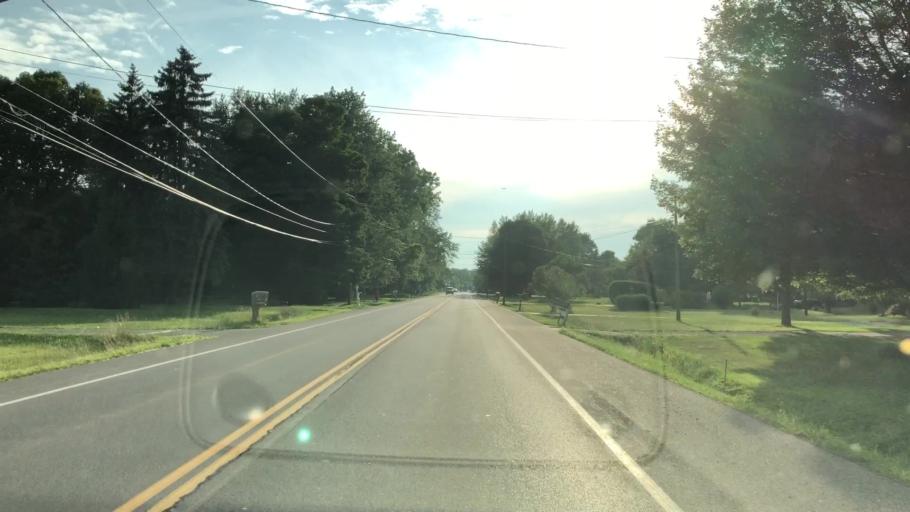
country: US
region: New York
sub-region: Erie County
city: Depew
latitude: 42.8925
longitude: -78.7124
